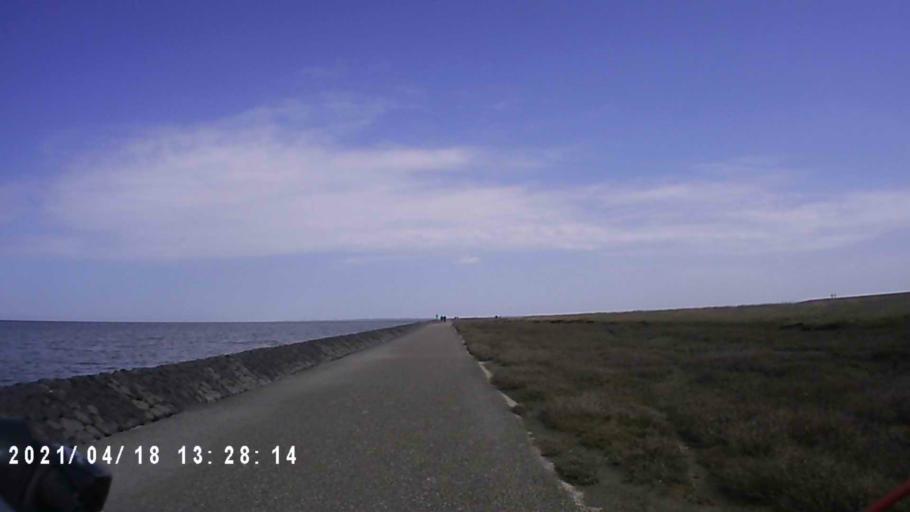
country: NL
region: Friesland
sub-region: Gemeente Dongeradeel
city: Anjum
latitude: 53.4071
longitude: 6.0893
